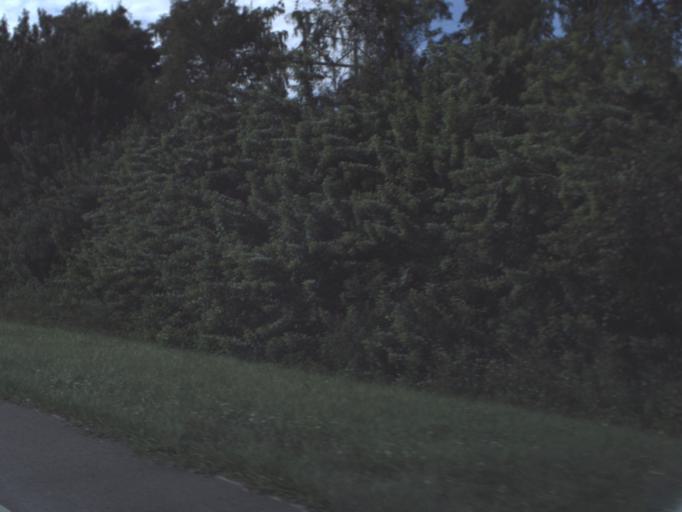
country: US
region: Florida
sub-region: Collier County
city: Immokalee
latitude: 26.3556
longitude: -81.3438
